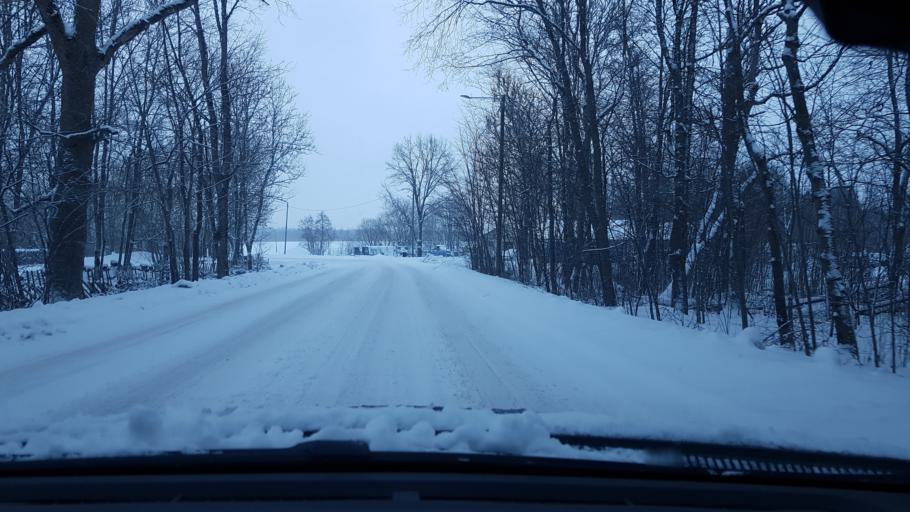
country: EE
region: Harju
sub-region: Anija vald
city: Kehra
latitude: 59.3830
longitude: 25.3018
